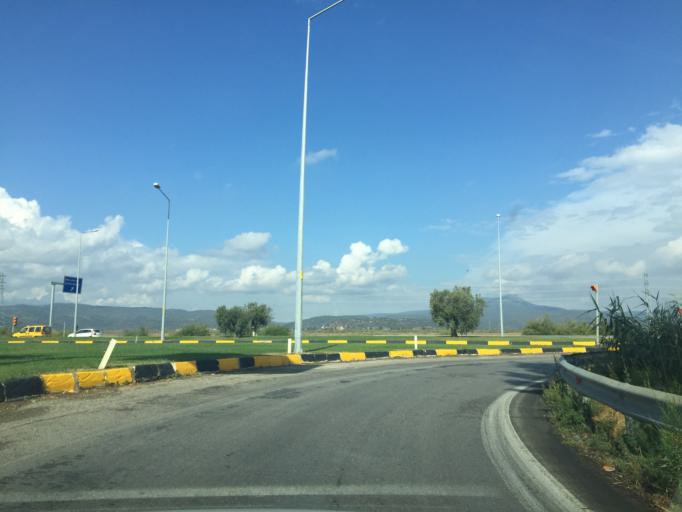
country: TR
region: Izmir
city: Selcuk
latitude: 37.9517
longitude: 27.2995
